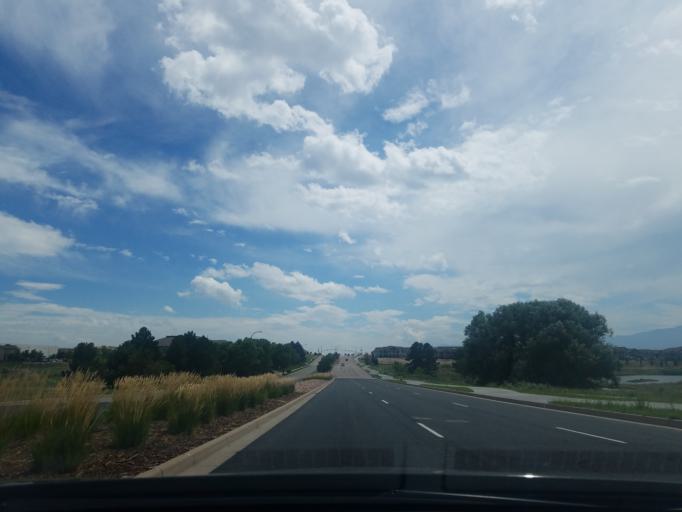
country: US
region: Colorado
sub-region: El Paso County
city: Gleneagle
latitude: 39.0001
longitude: -104.7980
